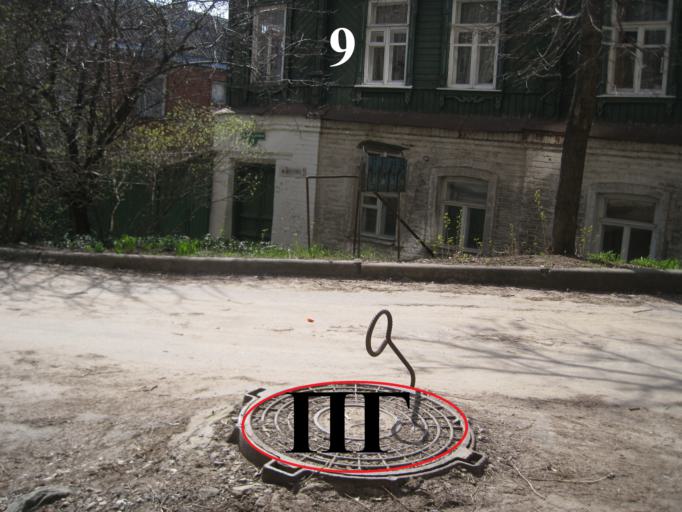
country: RU
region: Voronezj
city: Voronezh
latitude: 51.6574
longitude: 39.1958
